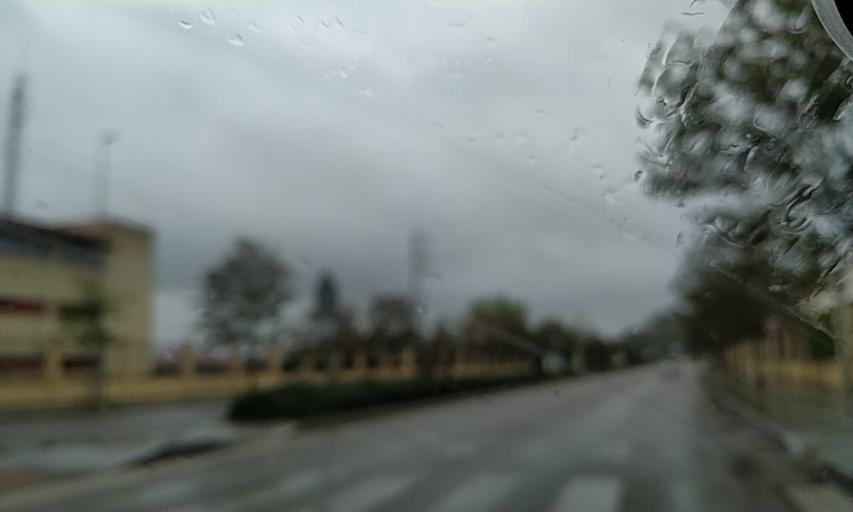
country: ES
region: Extremadura
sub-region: Provincia de Badajoz
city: Badajoz
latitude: 38.8949
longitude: -6.9703
